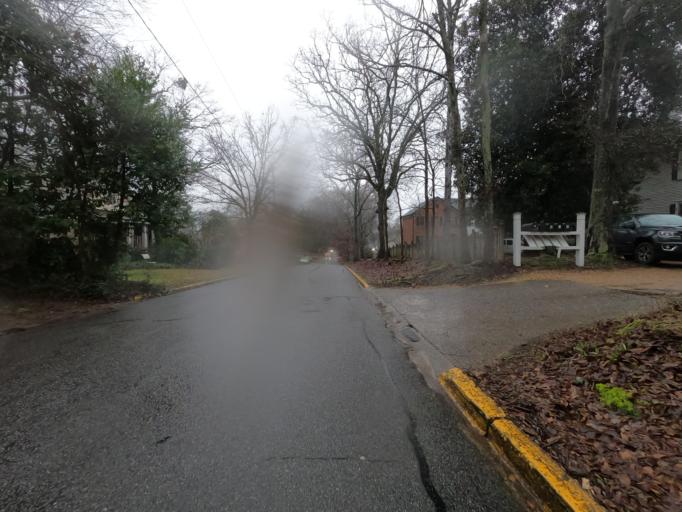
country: US
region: Georgia
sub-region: Clarke County
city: Athens
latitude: 33.9523
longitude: -83.3845
